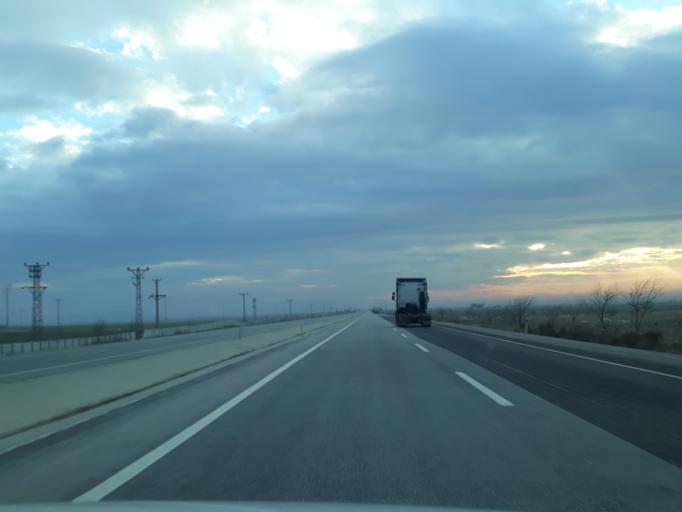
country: TR
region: Konya
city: Hotamis
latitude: 37.7107
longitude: 33.2817
